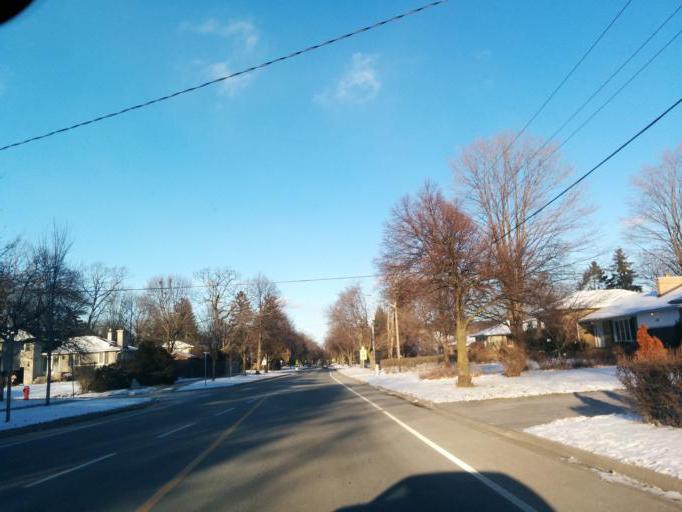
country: CA
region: Ontario
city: Mississauga
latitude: 43.5264
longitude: -79.6354
